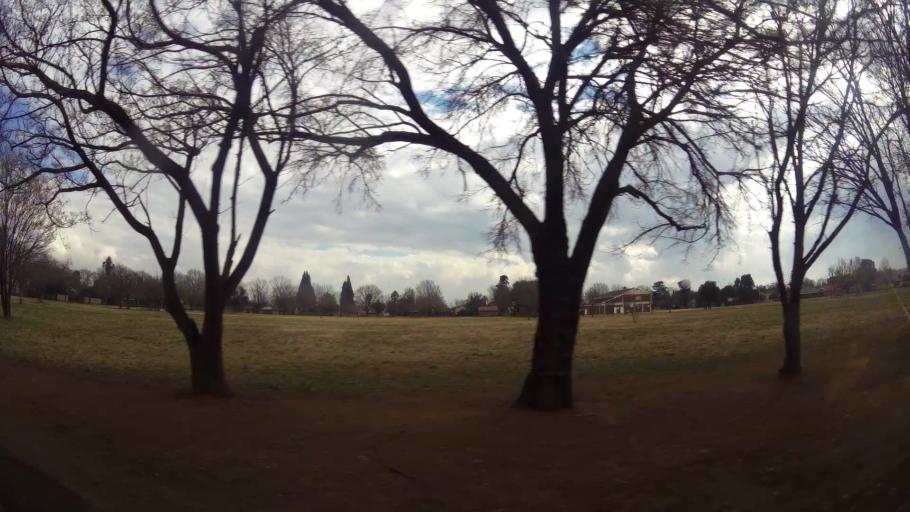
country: ZA
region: Gauteng
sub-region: Sedibeng District Municipality
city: Vereeniging
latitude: -26.6426
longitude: 27.9773
